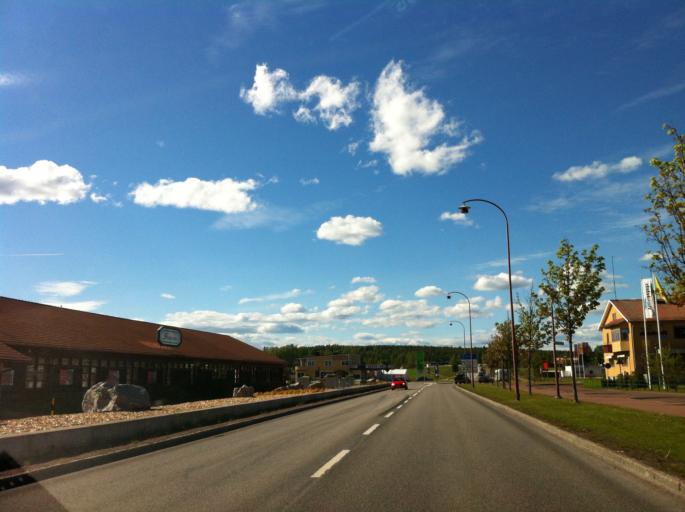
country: SE
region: Dalarna
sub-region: Rattviks Kommun
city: Raettvik
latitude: 60.8886
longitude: 15.1120
